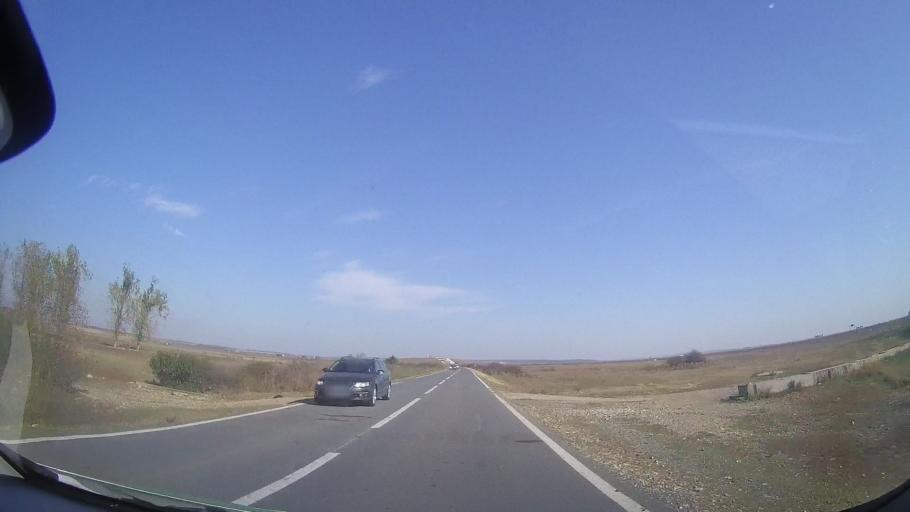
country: RO
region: Timis
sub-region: Comuna Belint
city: Belint
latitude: 45.7741
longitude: 21.7309
